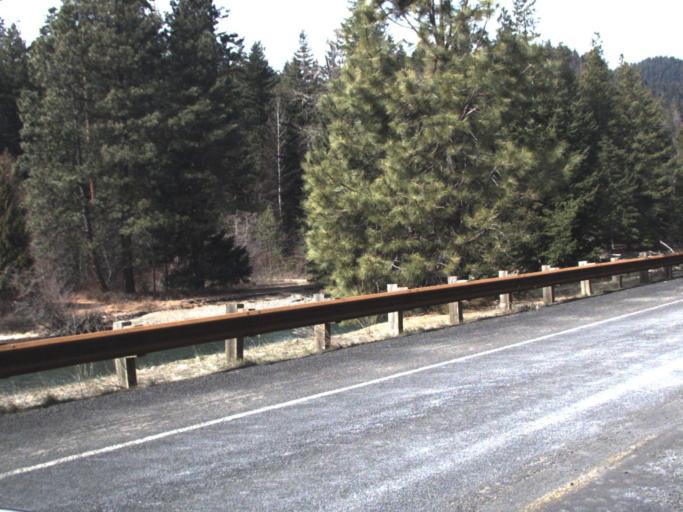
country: US
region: Washington
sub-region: Kittitas County
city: Cle Elum
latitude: 46.9621
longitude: -121.0833
